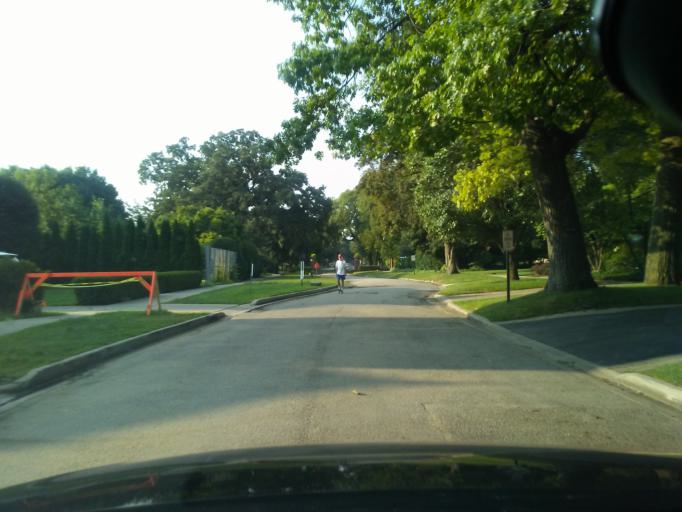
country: US
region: Illinois
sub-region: Cook County
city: Evanston
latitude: 42.0348
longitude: -87.6707
